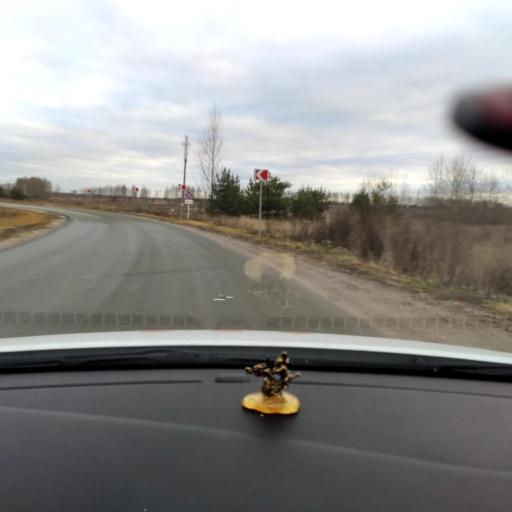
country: RU
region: Tatarstan
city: Stolbishchi
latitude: 55.6150
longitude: 49.1572
